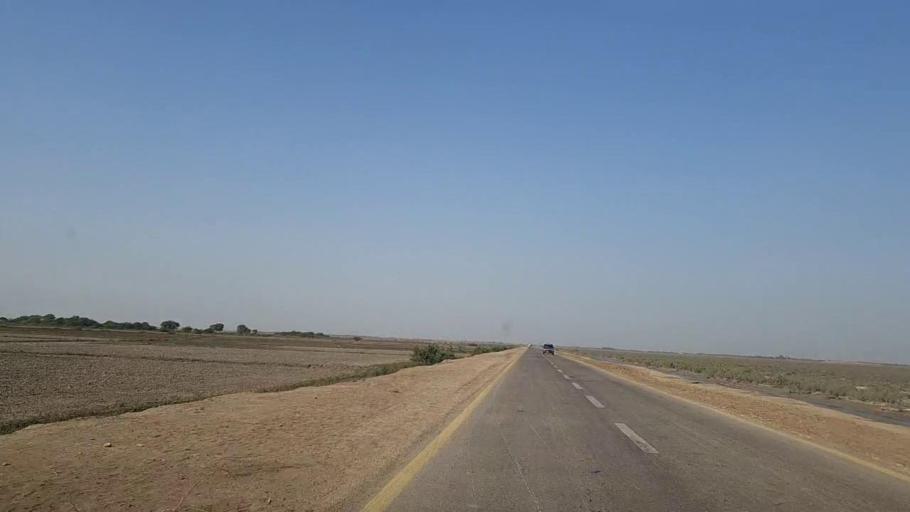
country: PK
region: Sindh
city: Jati
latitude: 24.4834
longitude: 68.3738
